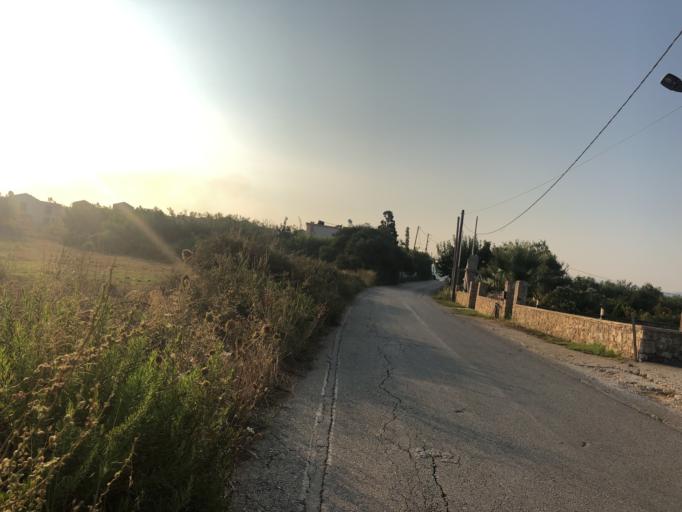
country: GR
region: Crete
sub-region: Nomos Chanias
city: Georgioupolis
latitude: 35.3494
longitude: 24.2834
